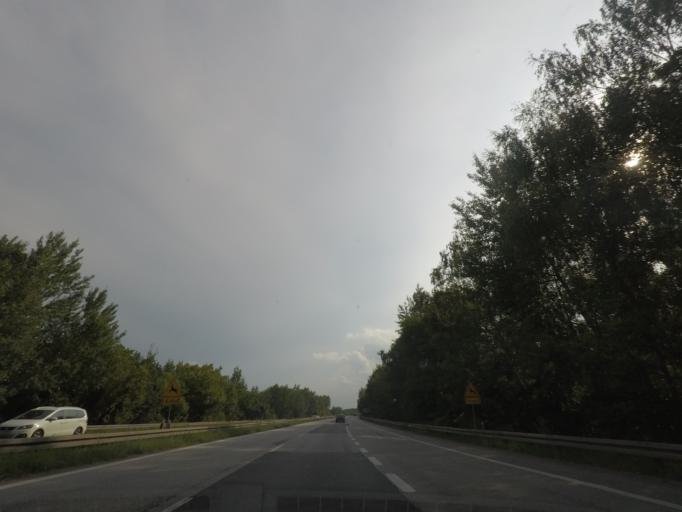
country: PL
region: Silesian Voivodeship
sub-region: Dabrowa Gornicza
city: Dabrowa Gornicza
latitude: 50.3135
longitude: 19.2342
